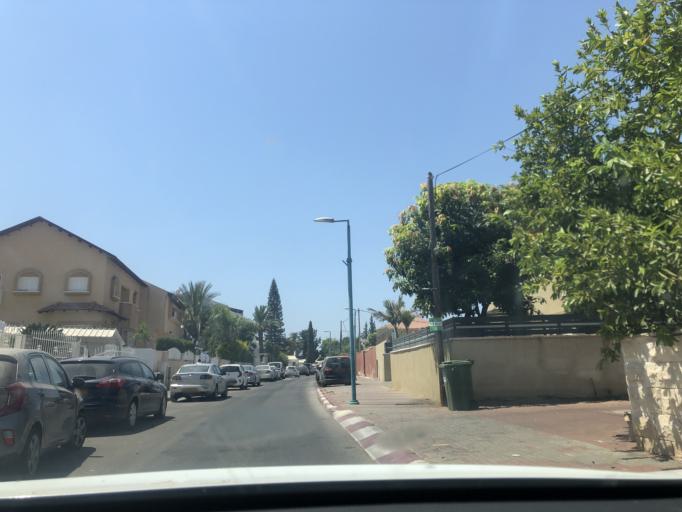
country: IL
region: Central District
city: Lod
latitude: 31.9405
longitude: 34.8831
